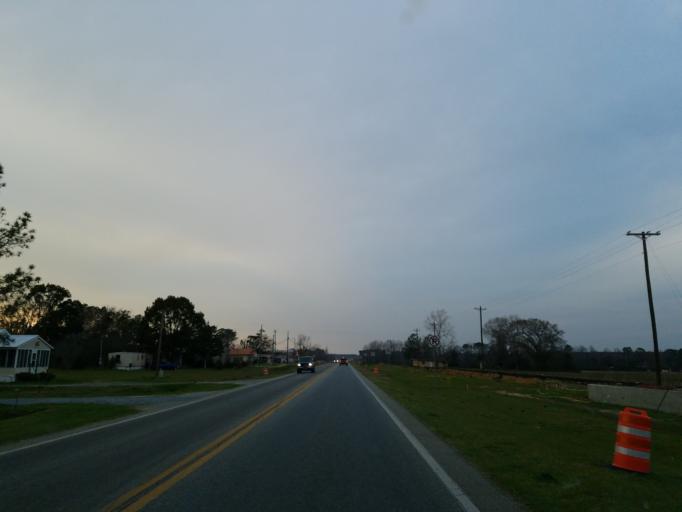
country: US
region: Georgia
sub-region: Colquitt County
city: Moultrie
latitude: 31.0724
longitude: -83.6200
